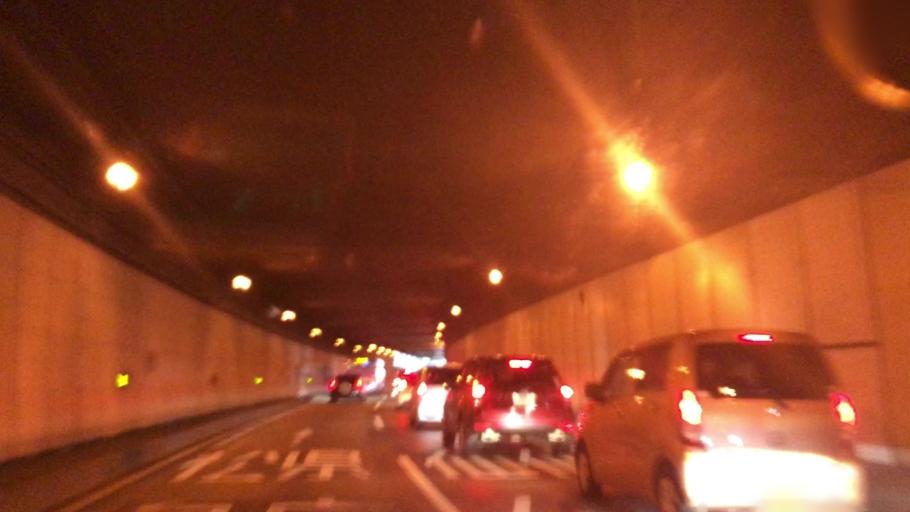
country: JP
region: Miyagi
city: Sendai
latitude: 38.2630
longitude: 140.8569
